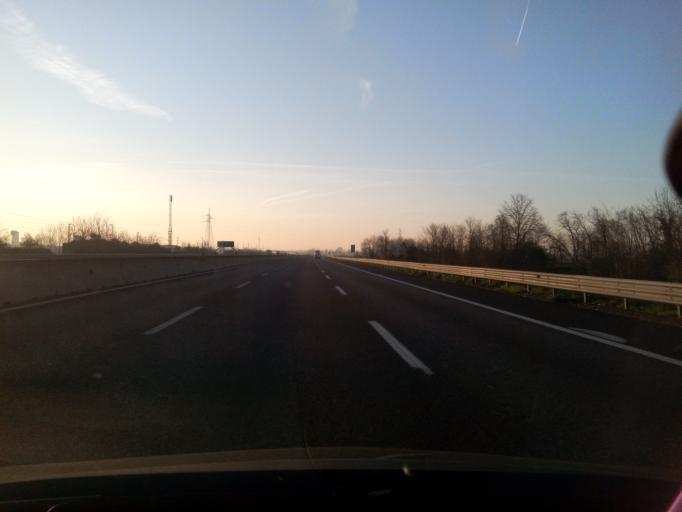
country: IT
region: Lombardy
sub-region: Provincia di Lodi
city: Lodi Vecchio
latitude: 45.3042
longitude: 9.4022
